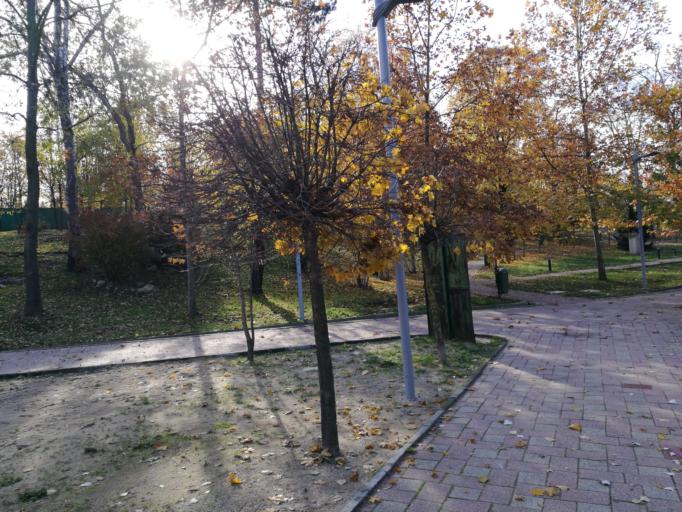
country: RO
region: Bucuresti
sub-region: Municipiul Bucuresti
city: Bucharest
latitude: 44.4714
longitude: 26.0910
